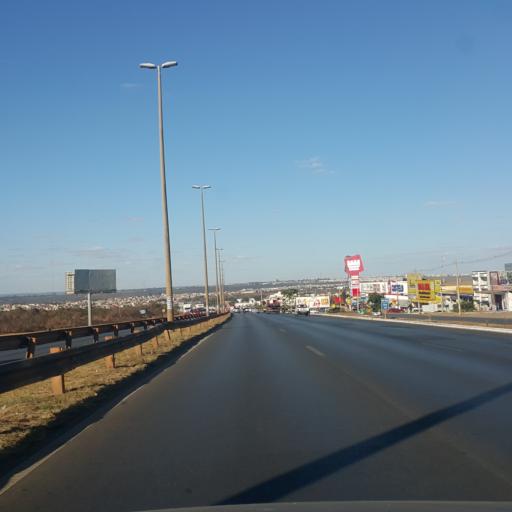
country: BR
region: Federal District
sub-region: Brasilia
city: Brasilia
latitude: -15.7906
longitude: -48.0269
